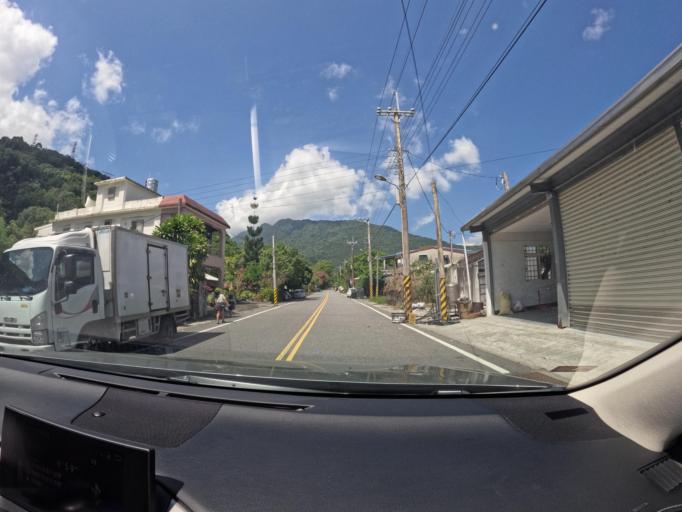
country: TW
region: Taiwan
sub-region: Hualien
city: Hualian
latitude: 23.6853
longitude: 121.4088
